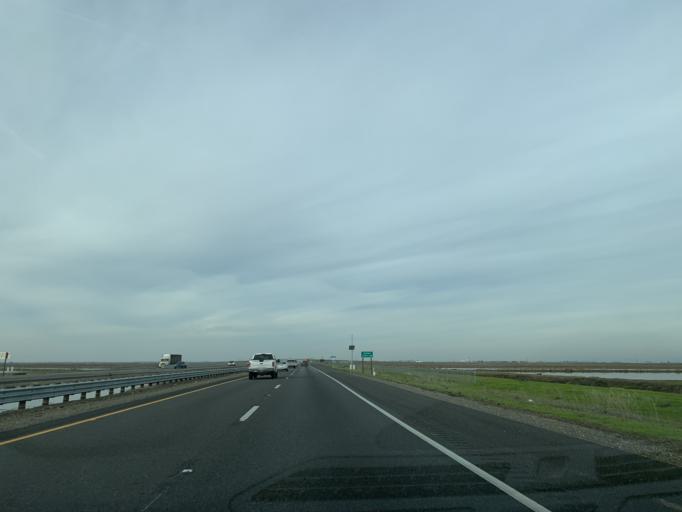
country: US
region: California
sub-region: Sacramento County
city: Elverta
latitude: 38.7356
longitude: -121.5404
